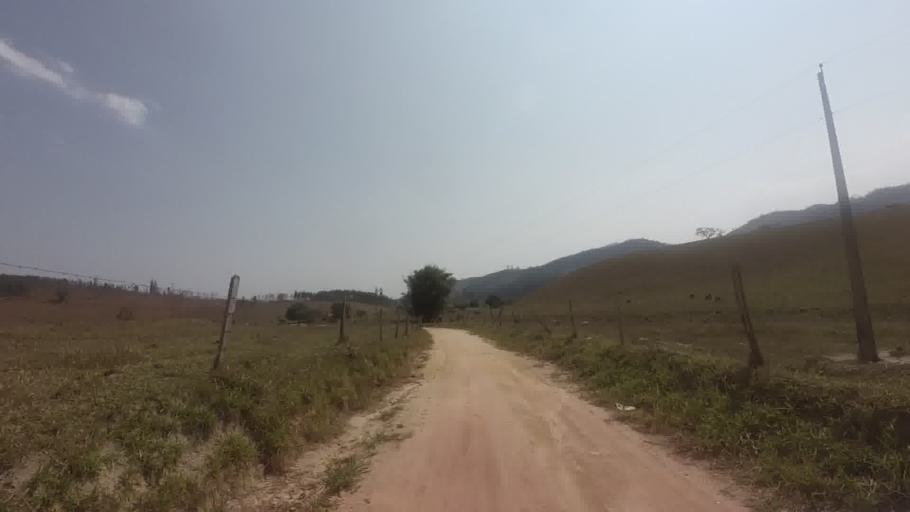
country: BR
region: Espirito Santo
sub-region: Sao Jose Do Calcado
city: Sao Jose do Calcado
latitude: -21.0377
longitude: -41.5255
